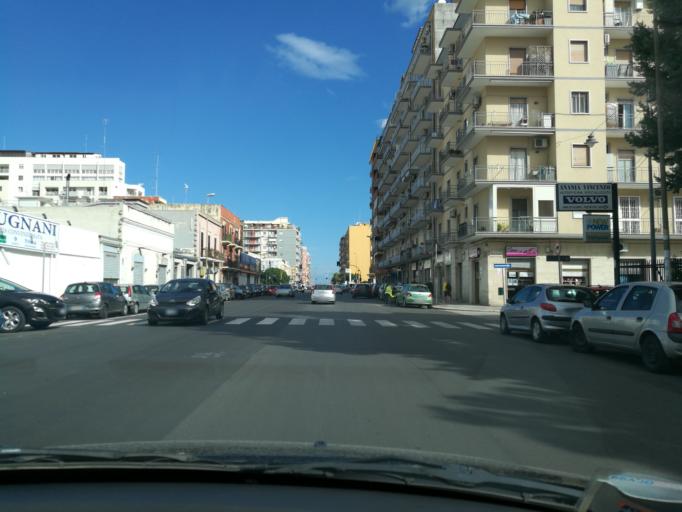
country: IT
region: Apulia
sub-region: Provincia di Bari
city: Bari
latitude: 41.1240
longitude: 16.8518
